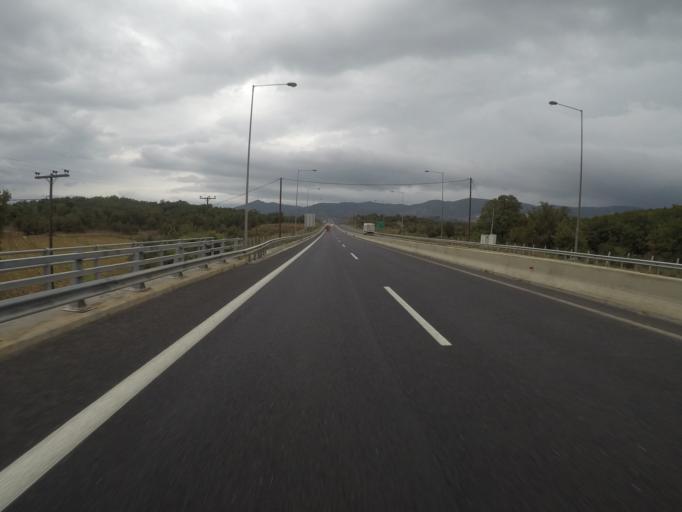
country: GR
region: Peloponnese
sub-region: Nomos Arkadias
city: Megalopoli
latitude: 37.3672
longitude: 22.1536
